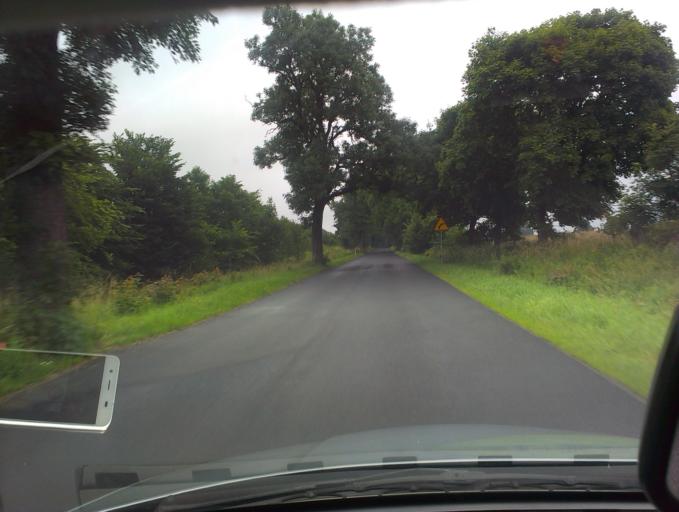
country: PL
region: West Pomeranian Voivodeship
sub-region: Powiat szczecinecki
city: Barwice
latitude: 53.7636
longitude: 16.3755
